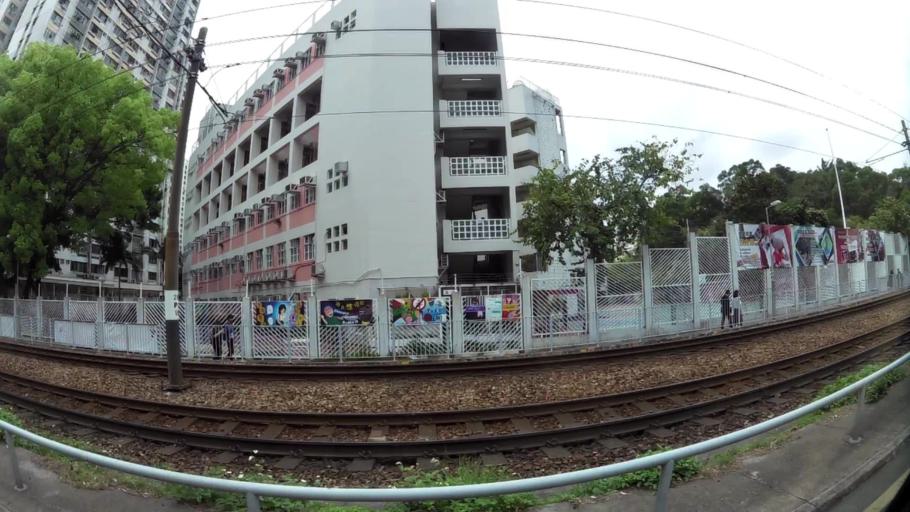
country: HK
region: Tuen Mun
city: Tuen Mun
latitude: 22.3896
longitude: 113.9752
